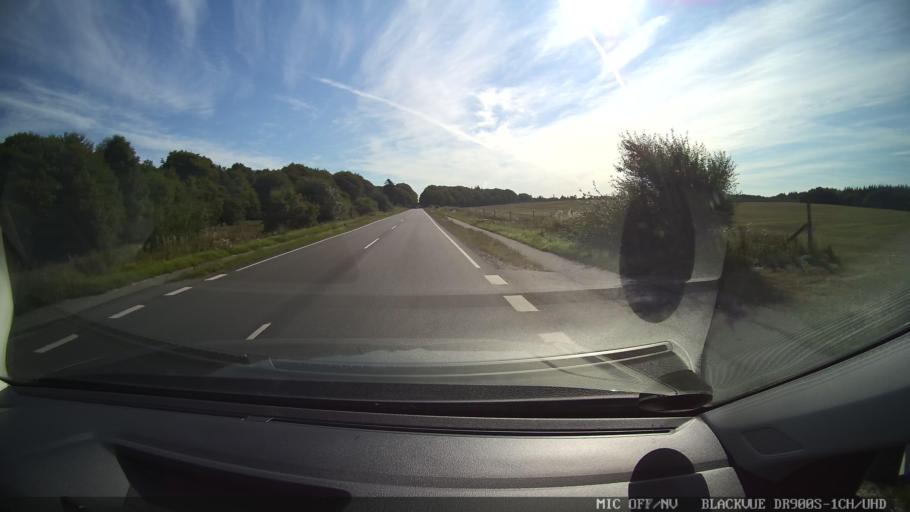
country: DK
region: North Denmark
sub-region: Mariagerfjord Kommune
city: Arden
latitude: 56.7834
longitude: 9.7352
